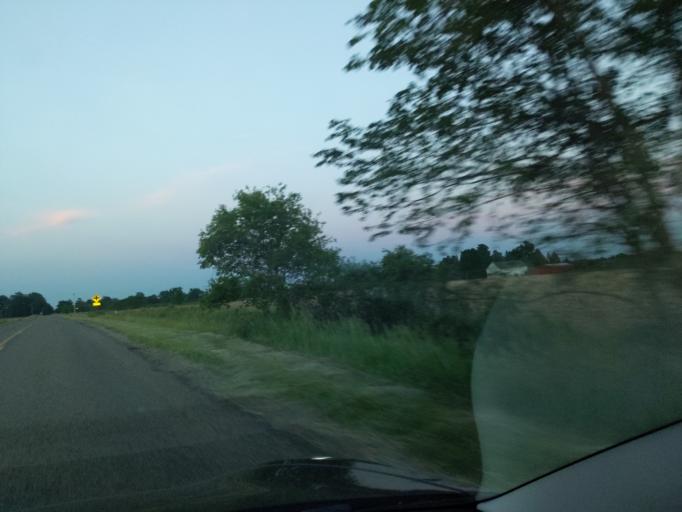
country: US
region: Michigan
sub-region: Eaton County
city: Olivet
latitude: 42.5390
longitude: -84.9580
